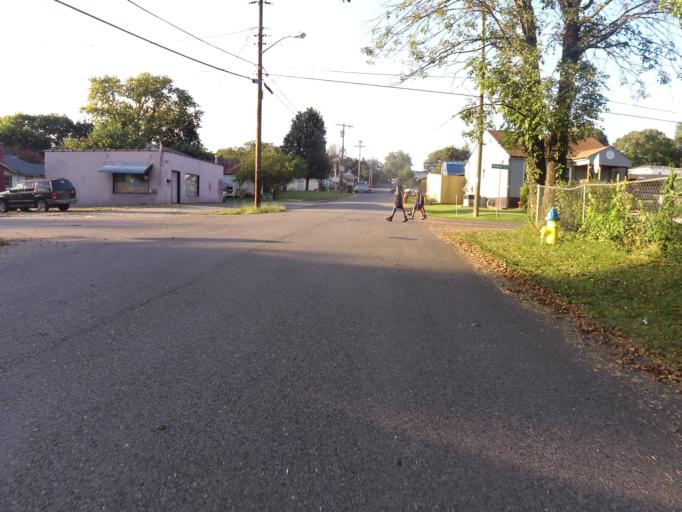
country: US
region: Tennessee
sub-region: Knox County
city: Knoxville
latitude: 35.9522
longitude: -83.9687
